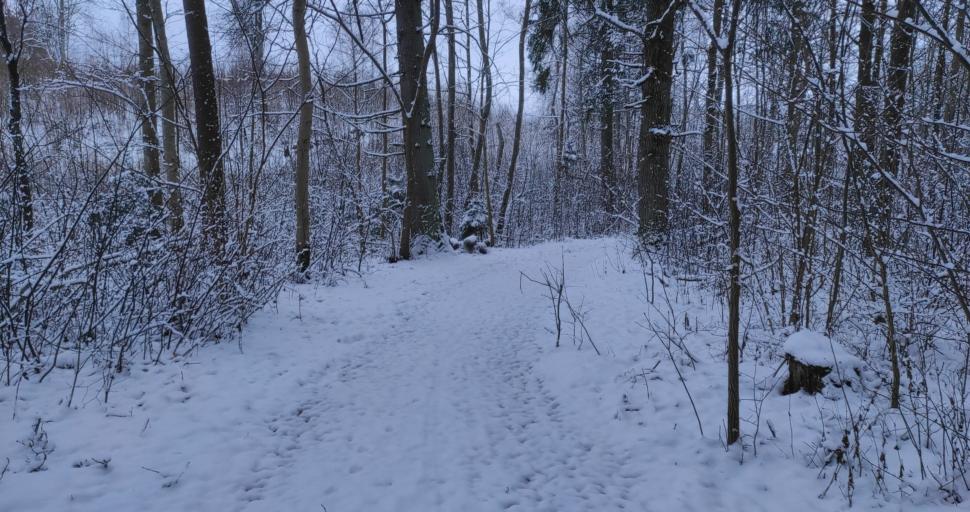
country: LV
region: Alsunga
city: Alsunga
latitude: 56.9841
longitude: 21.5837
